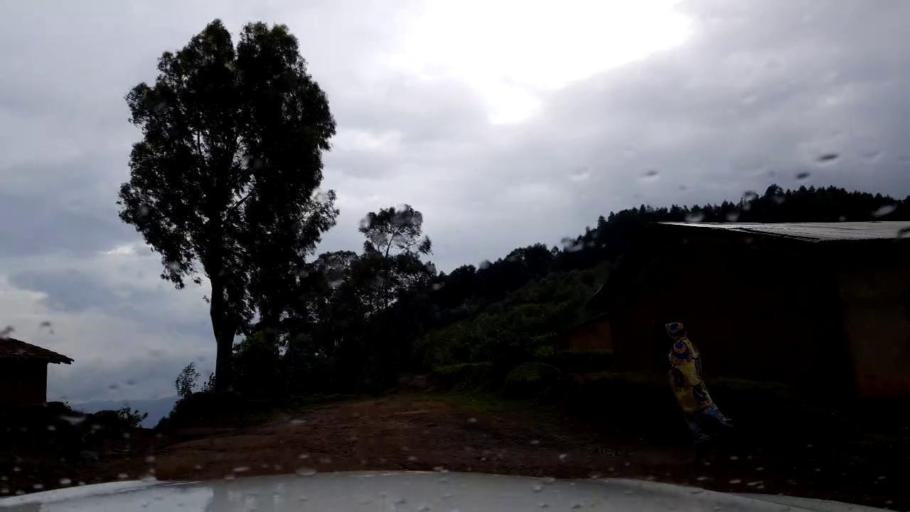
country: RW
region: Western Province
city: Kibuye
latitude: -2.0252
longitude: 29.4551
